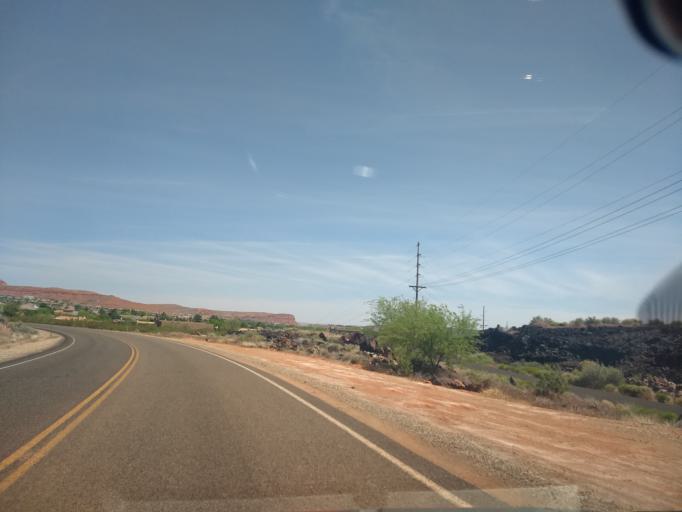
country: US
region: Utah
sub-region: Washington County
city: Santa Clara
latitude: 37.1417
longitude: -113.6425
